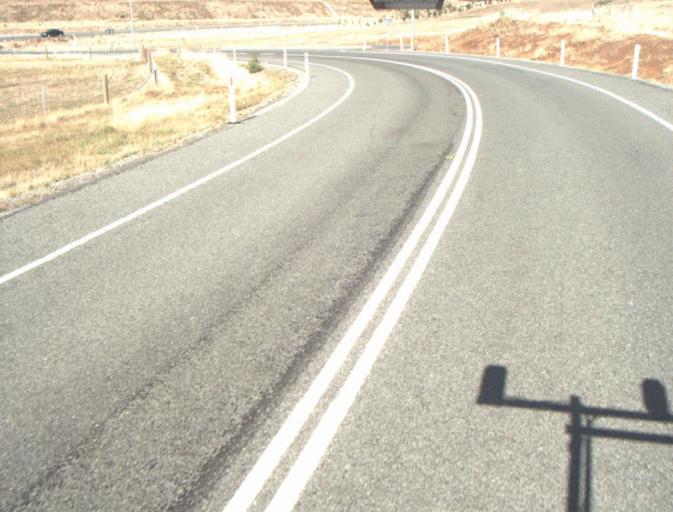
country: AU
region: Tasmania
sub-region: Launceston
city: Mayfield
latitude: -41.3535
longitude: 147.1014
